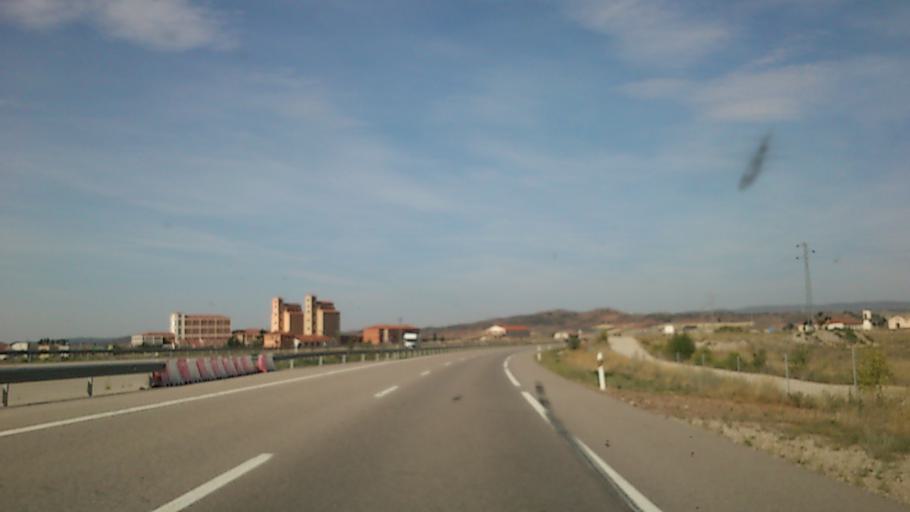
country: ES
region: Aragon
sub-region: Provincia de Teruel
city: Calamocha
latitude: 40.9000
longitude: -1.3019
